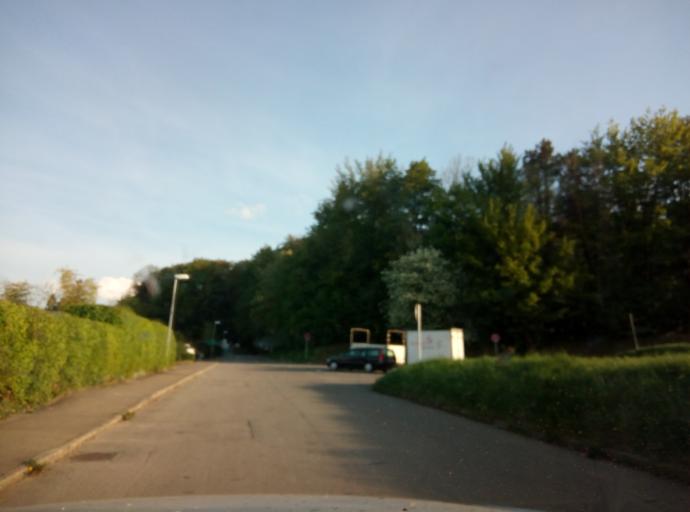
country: DE
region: Baden-Wuerttemberg
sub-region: Tuebingen Region
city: Tuebingen
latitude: 48.5064
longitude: 9.0718
